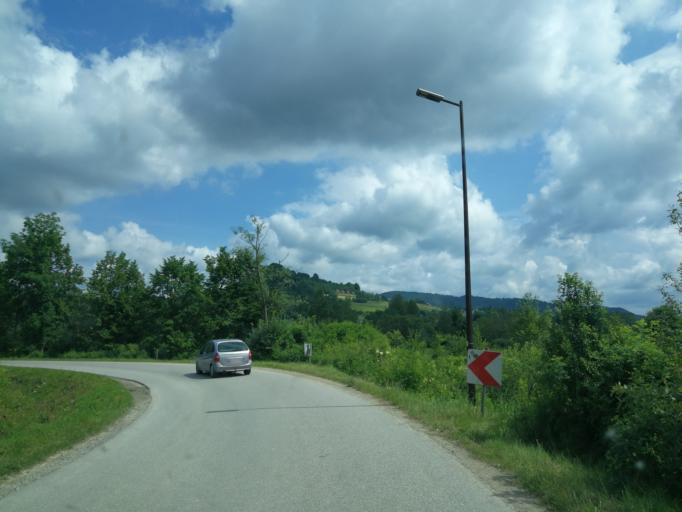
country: PL
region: Subcarpathian Voivodeship
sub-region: Powiat leski
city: Polanczyk
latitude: 49.4154
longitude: 22.4430
